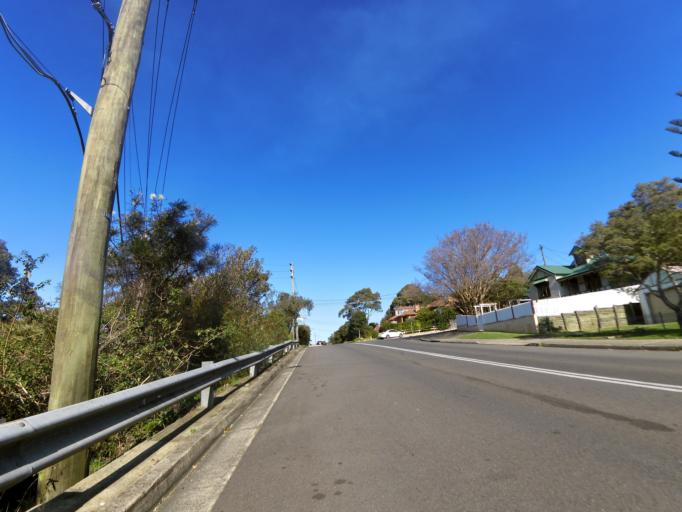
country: AU
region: New South Wales
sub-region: Sutherland Shire
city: Como
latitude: -34.0035
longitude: 151.0686
